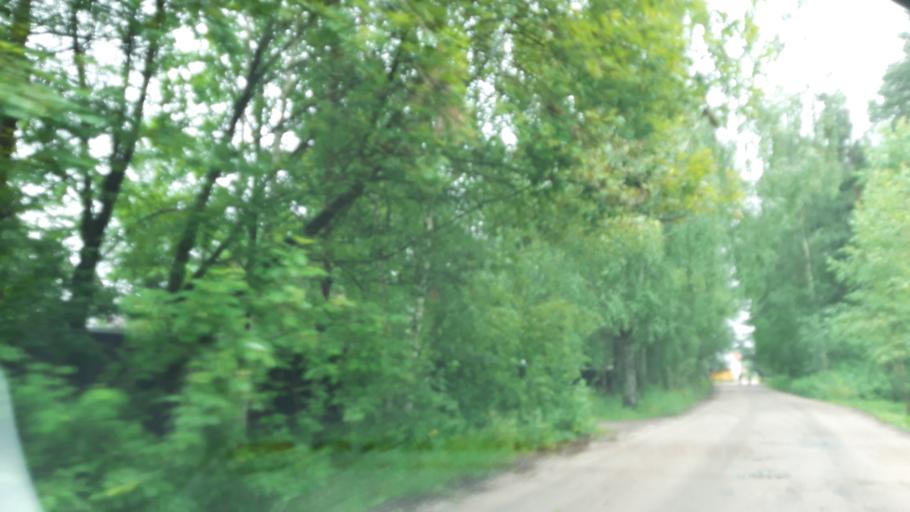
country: RU
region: Tverskaya
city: Konakovo
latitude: 56.6557
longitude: 36.6567
